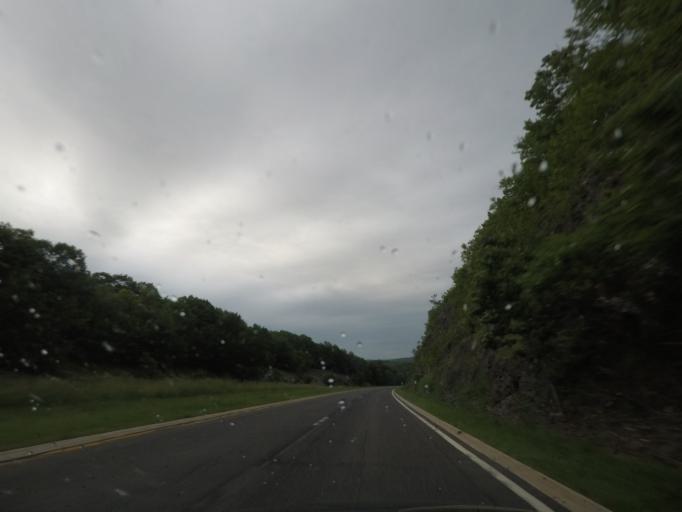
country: US
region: New York
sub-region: Columbia County
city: Chatham
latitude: 42.3231
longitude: -73.5750
